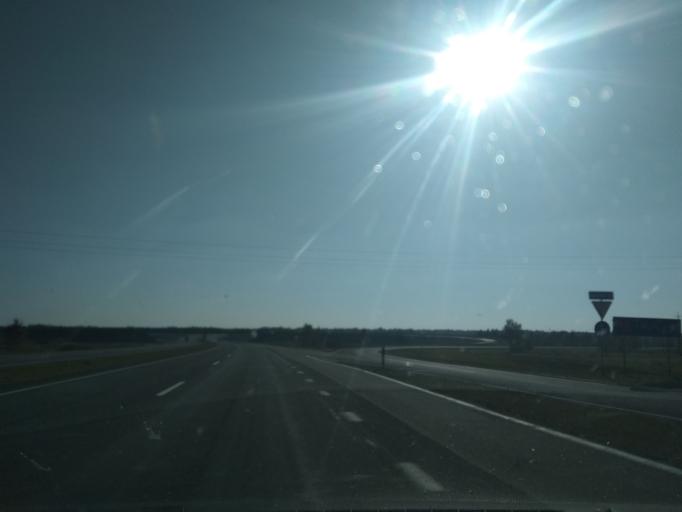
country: BY
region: Brest
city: Horad Kobryn
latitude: 52.2215
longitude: 24.4225
